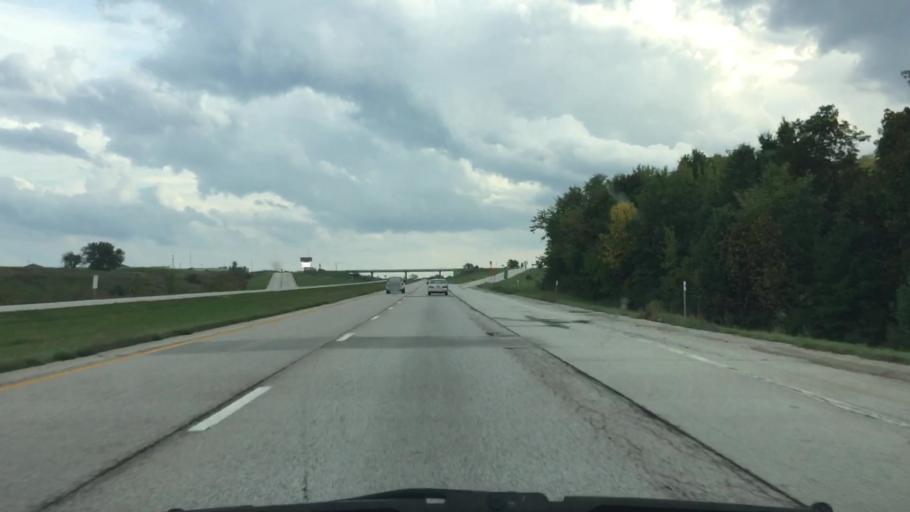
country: US
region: Missouri
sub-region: Clinton County
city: Cameron
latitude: 39.7364
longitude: -94.2206
